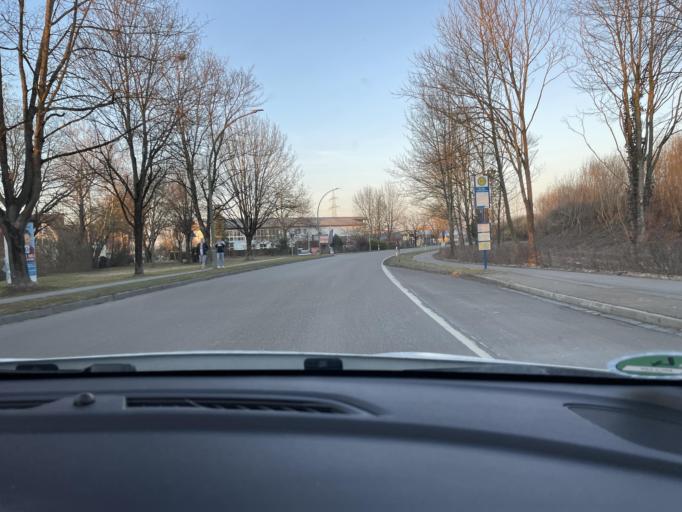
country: DE
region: Bavaria
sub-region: Swabia
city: Meitingen
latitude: 48.5529
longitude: 10.8573
